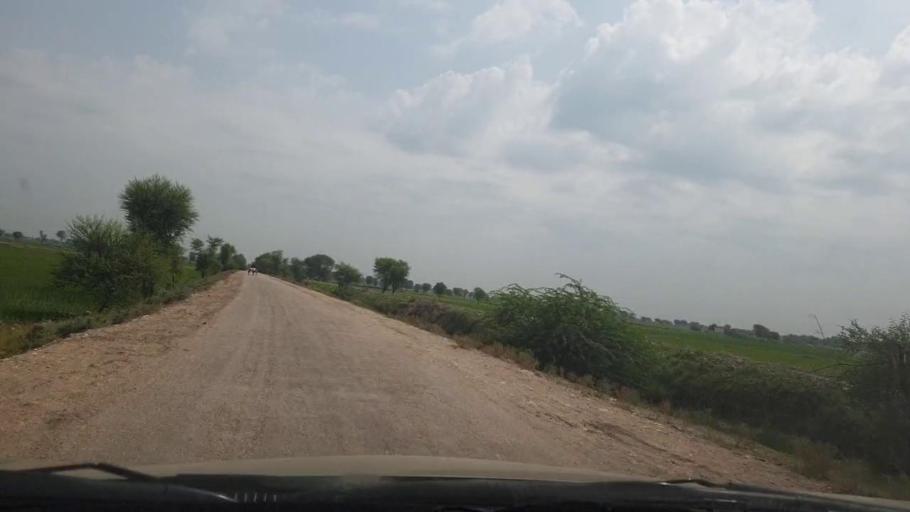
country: PK
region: Sindh
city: Miro Khan
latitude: 27.6830
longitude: 68.1880
